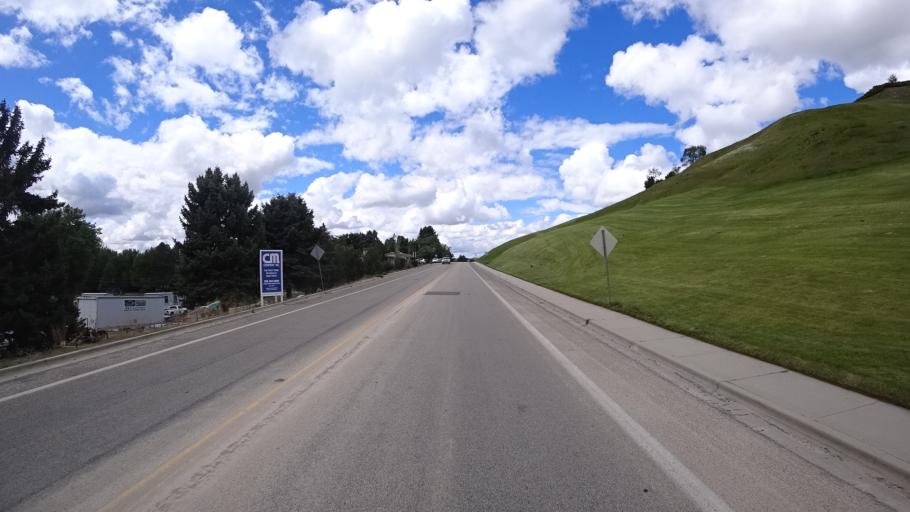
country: US
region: Idaho
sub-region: Ada County
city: Boise
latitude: 43.6510
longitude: -116.1957
